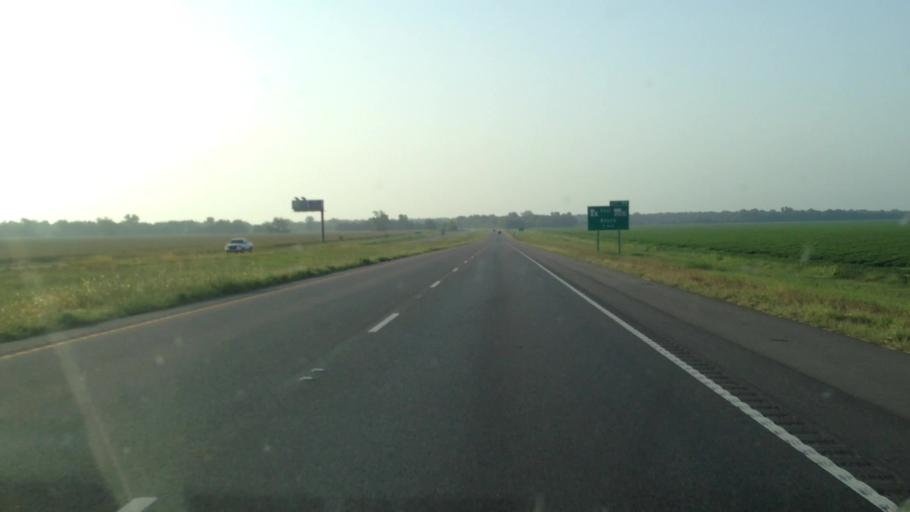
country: US
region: Louisiana
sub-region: Rapides Parish
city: Boyce
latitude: 31.3903
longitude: -92.6899
